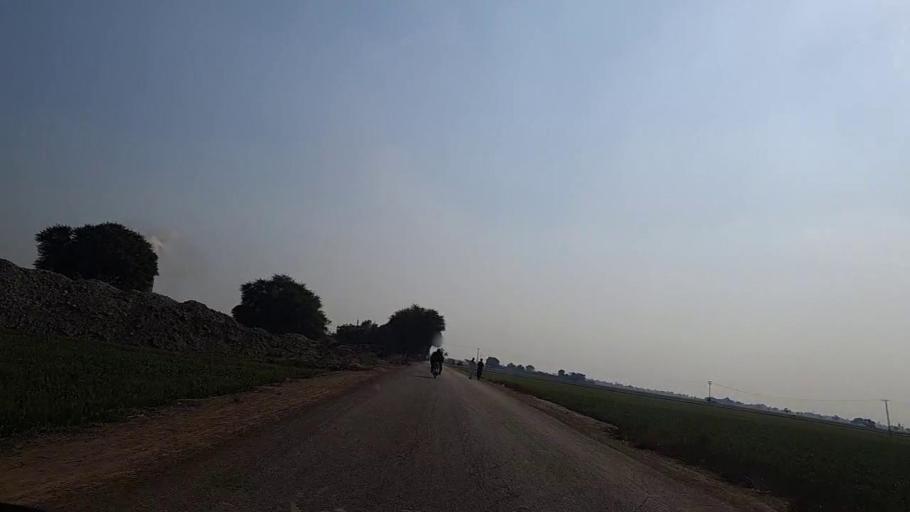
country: PK
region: Sindh
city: Sakrand
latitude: 26.1000
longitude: 68.2906
